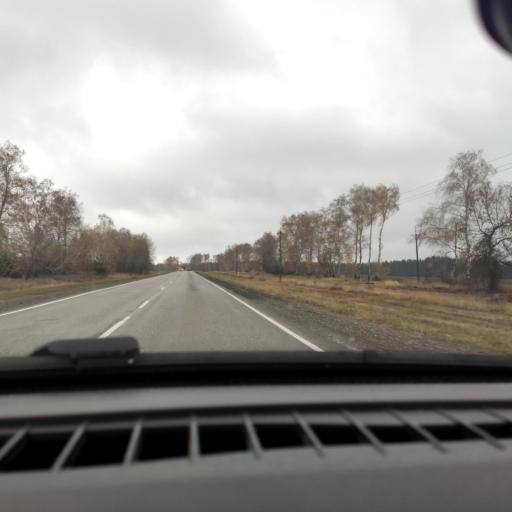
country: RU
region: Voronezj
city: Uryv-Pokrovka
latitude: 51.0616
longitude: 38.9926
